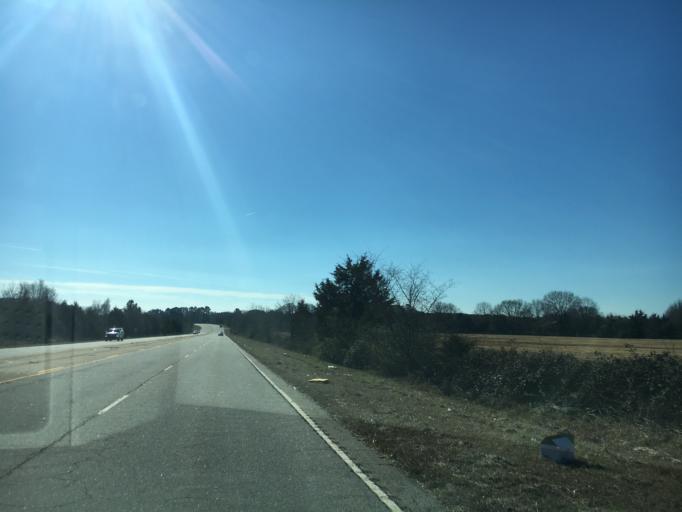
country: US
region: South Carolina
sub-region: Anderson County
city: Homeland Park
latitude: 34.3991
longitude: -82.6889
